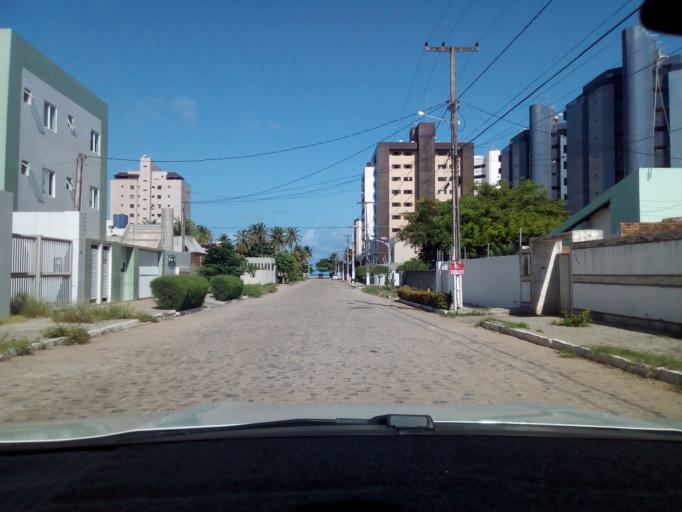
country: BR
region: Paraiba
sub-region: Cabedelo
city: Cabedelo
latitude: -7.0423
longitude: -34.8433
